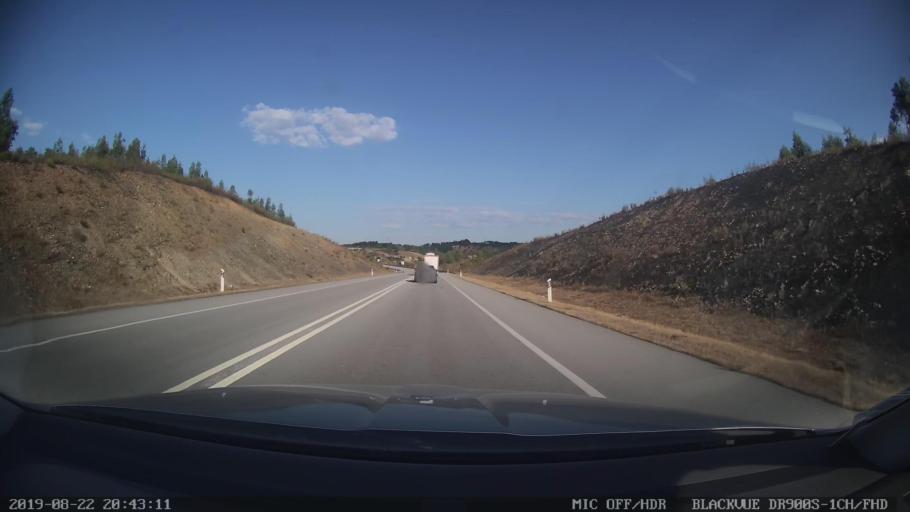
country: PT
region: Castelo Branco
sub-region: Proenca-A-Nova
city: Proenca-a-Nova
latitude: 39.6990
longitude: -7.8278
